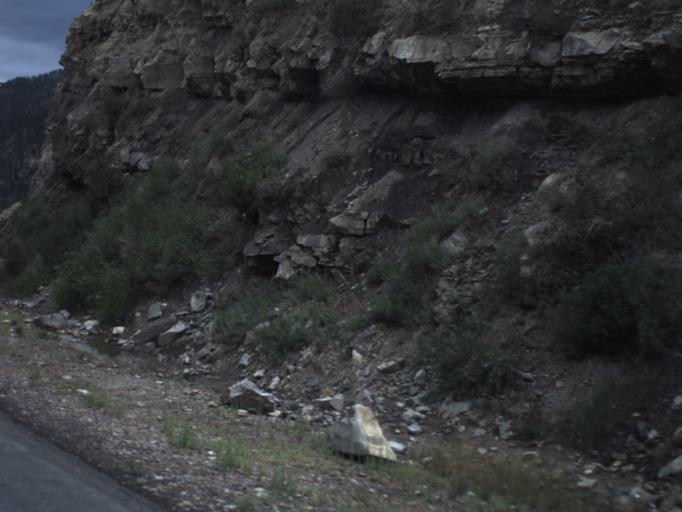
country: US
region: Utah
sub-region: Carbon County
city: Helper
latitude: 39.7993
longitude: -110.9322
